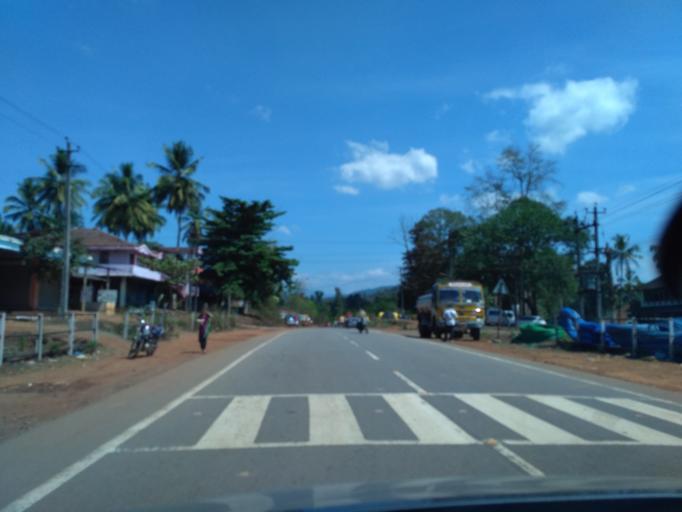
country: IN
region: Karnataka
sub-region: Dakshina Kannada
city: Sulya
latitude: 12.5195
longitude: 75.4695
